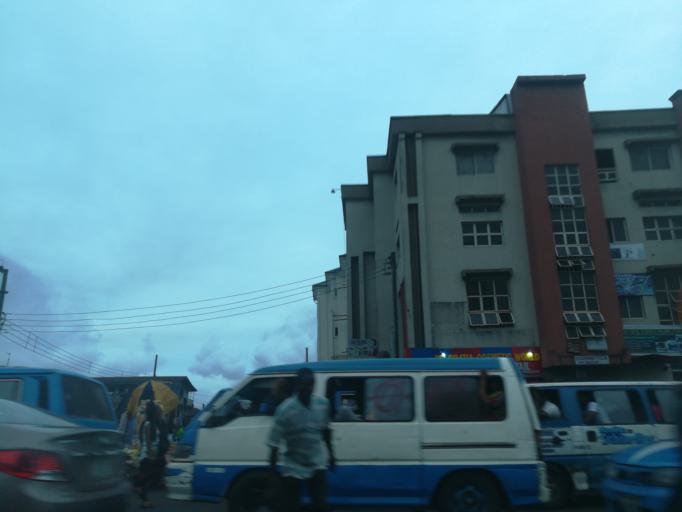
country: NG
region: Rivers
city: Port Harcourt
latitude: 4.8016
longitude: 6.9905
